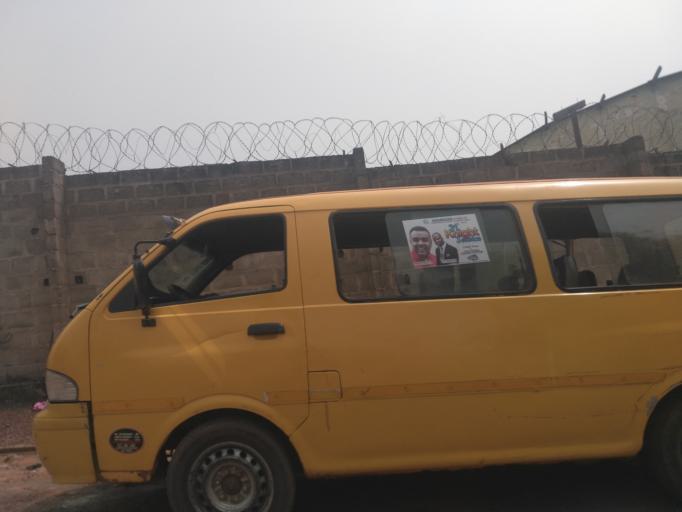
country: GH
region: Ashanti
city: Kumasi
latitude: 6.6856
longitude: -1.6223
